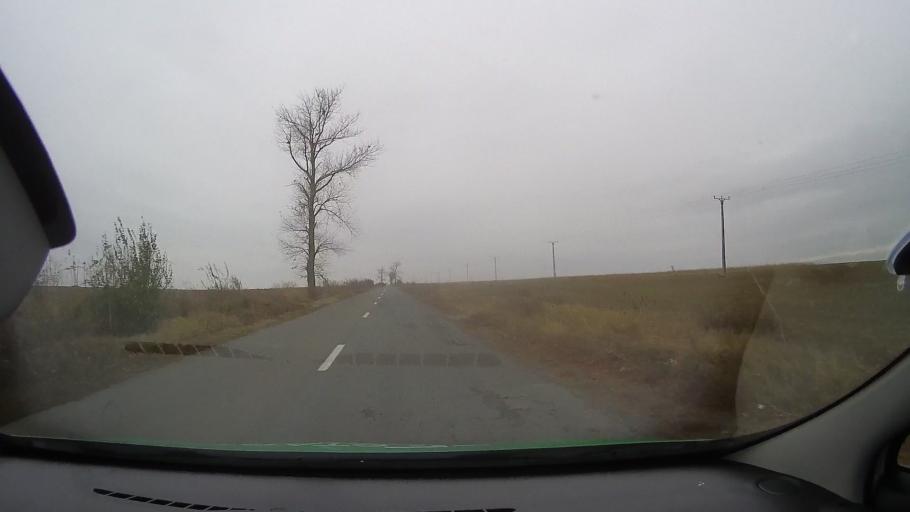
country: RO
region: Constanta
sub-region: Comuna Pantelimon
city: Pantelimon
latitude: 44.5626
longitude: 28.3204
